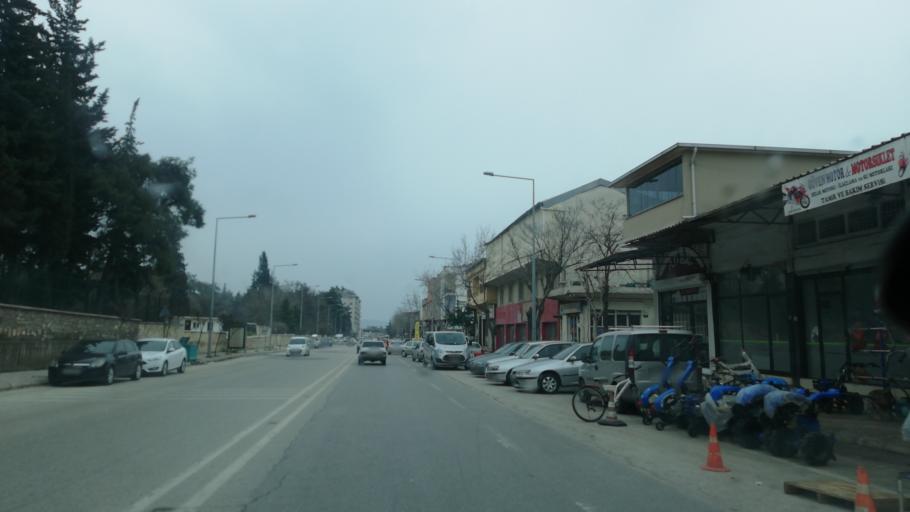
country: TR
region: Kahramanmaras
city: Kahramanmaras
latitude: 37.5747
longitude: 36.9371
